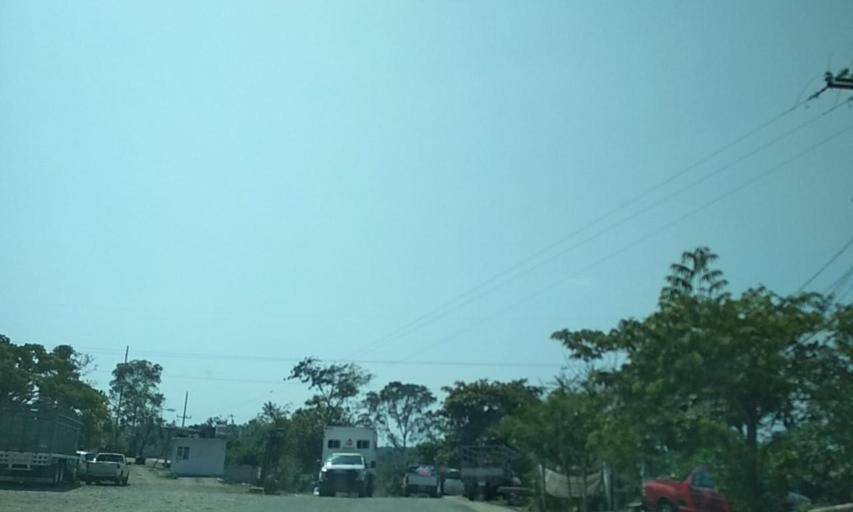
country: MX
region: Veracruz
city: Agua Dulce
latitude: 20.3732
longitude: -97.1835
